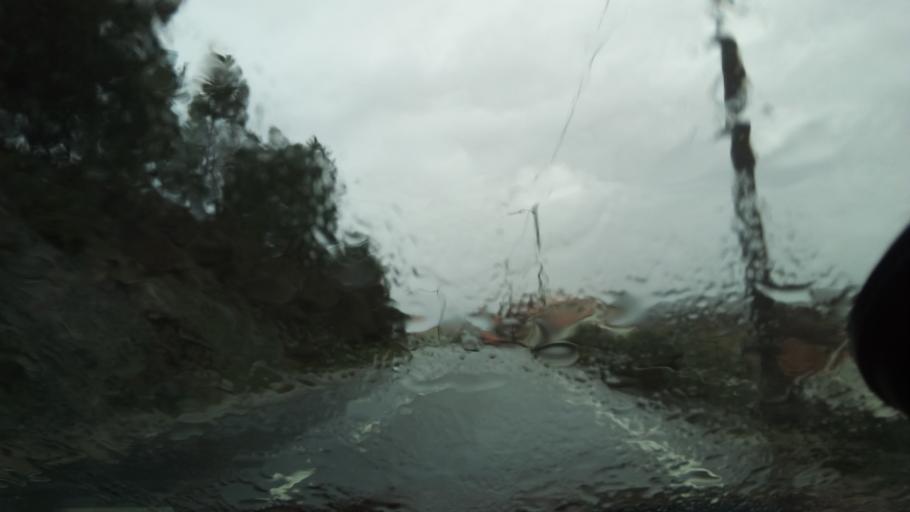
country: PT
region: Guarda
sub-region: Fornos de Algodres
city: Fornos de Algodres
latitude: 40.5190
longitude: -7.5806
